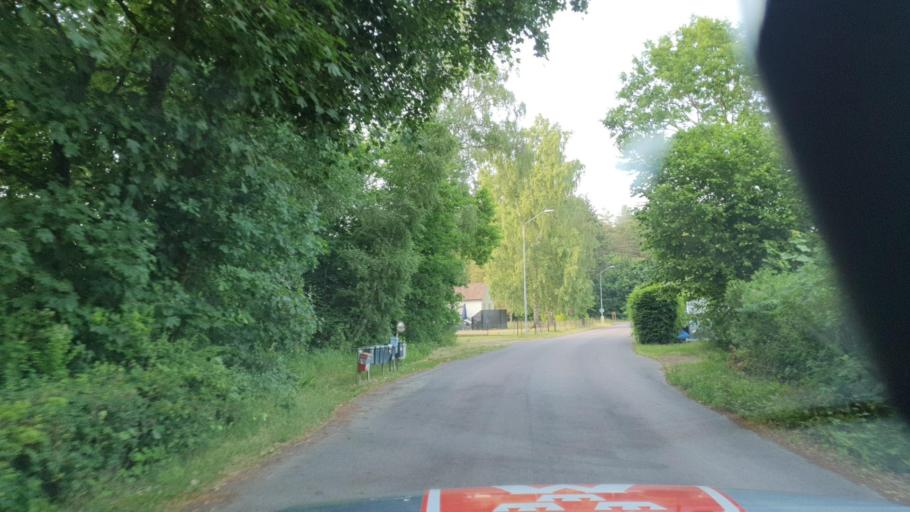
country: SE
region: Kalmar
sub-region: Kalmar Kommun
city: Ljungbyholm
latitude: 56.5910
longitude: 16.1493
